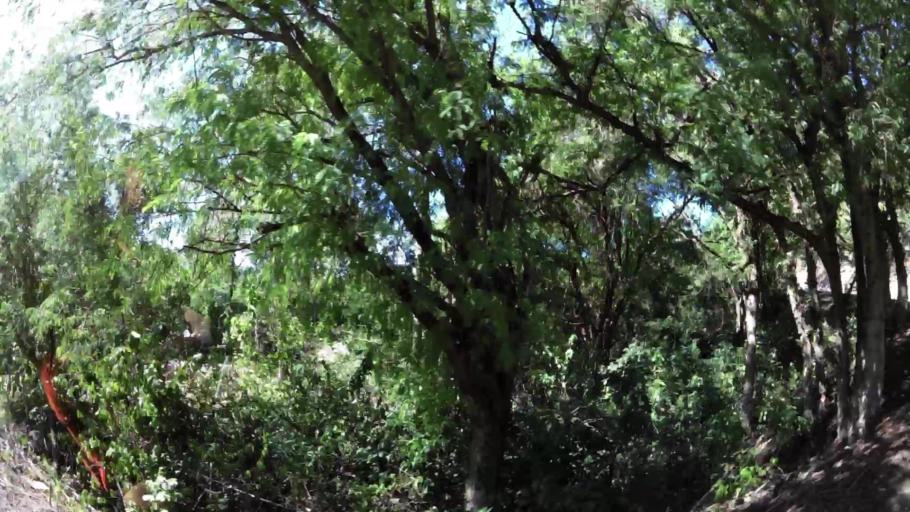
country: AG
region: Saint Paul
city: Falmouth
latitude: 17.0075
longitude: -61.7575
